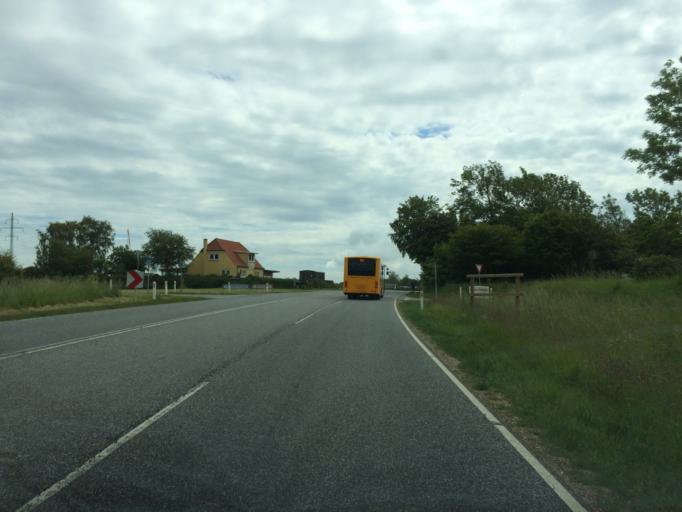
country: DK
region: Zealand
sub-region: Odsherred Kommune
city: Hojby
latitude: 55.9510
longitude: 11.4895
